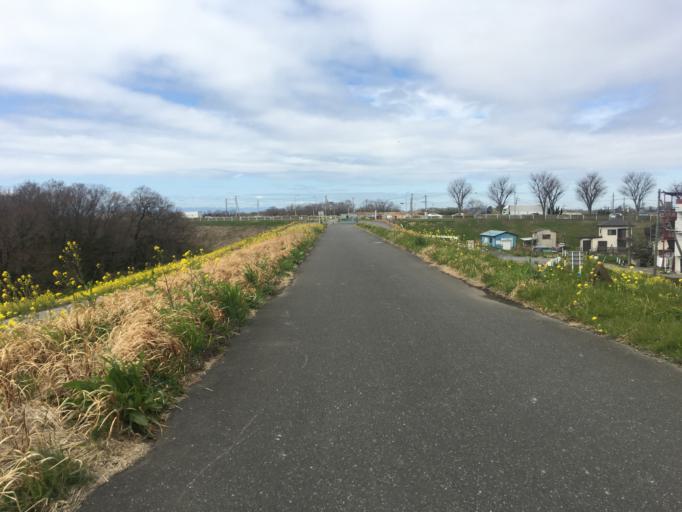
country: JP
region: Saitama
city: Shiki
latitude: 35.8588
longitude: 139.5982
